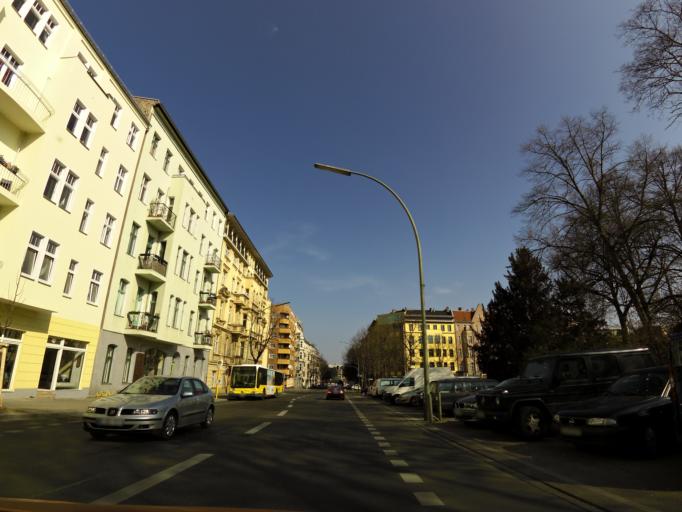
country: DE
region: Berlin
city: Bezirk Kreuzberg
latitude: 52.4886
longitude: 13.3767
